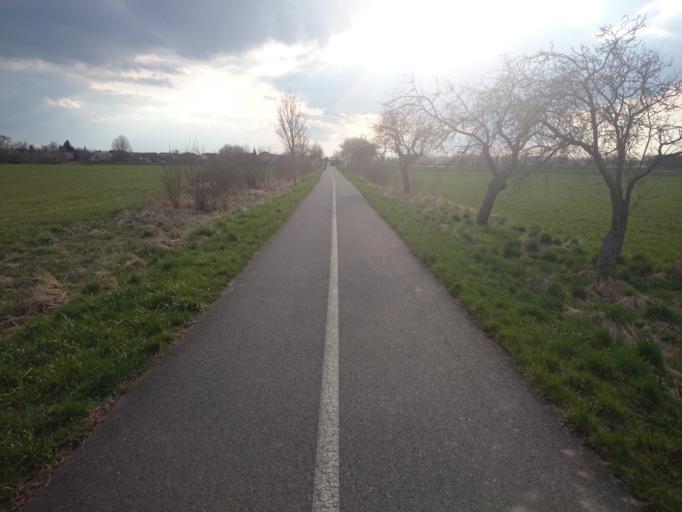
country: CZ
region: Pardubicky
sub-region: Okres Pardubice
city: Pardubice
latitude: 50.0046
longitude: 15.7596
